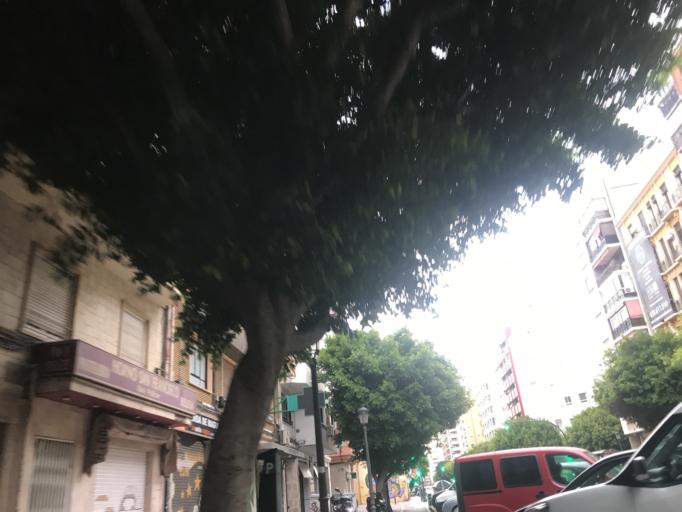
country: ES
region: Valencia
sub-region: Provincia de Valencia
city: Valencia
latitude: 39.4613
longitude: -0.3826
